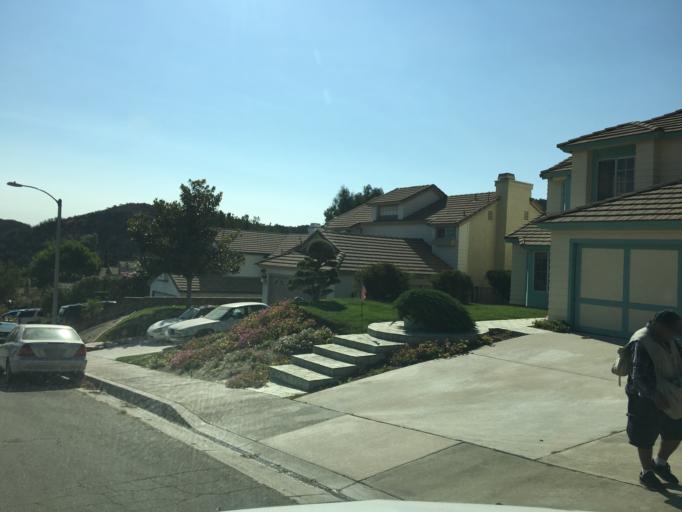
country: US
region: California
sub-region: Los Angeles County
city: Castaic
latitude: 34.4864
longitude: -118.6368
